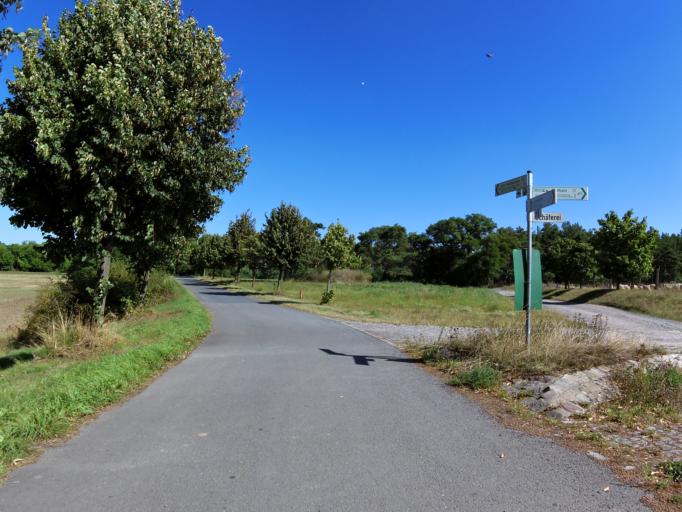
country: DE
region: Saxony
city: Strehla
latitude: 51.3817
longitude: 13.2616
